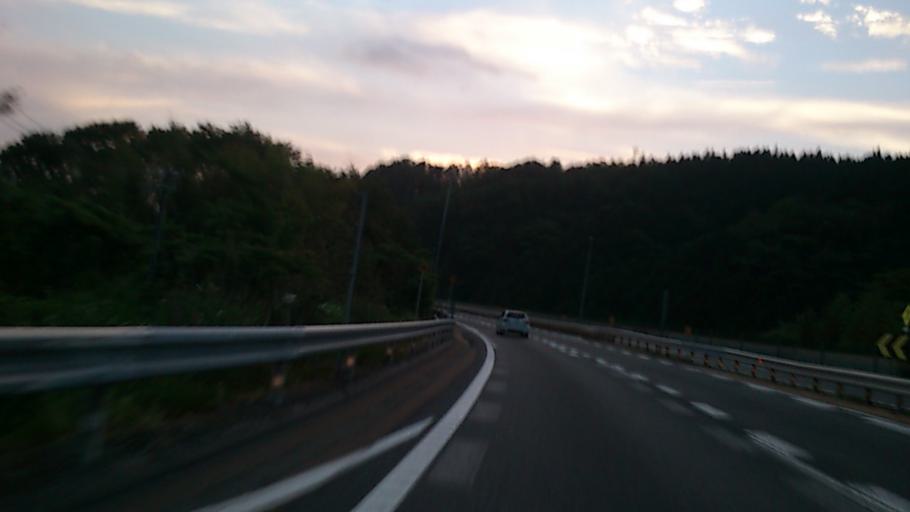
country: JP
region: Gifu
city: Nakatsugawa
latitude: 35.5125
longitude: 137.5838
